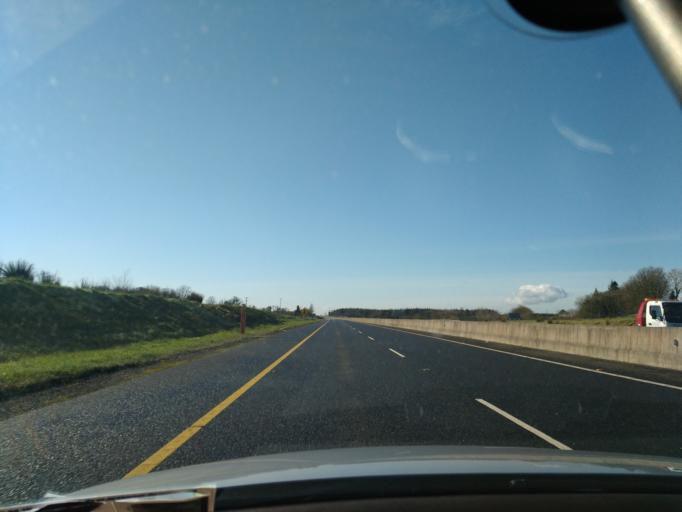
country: IE
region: Munster
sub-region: North Tipperary
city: Newport
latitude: 52.7564
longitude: -8.4096
